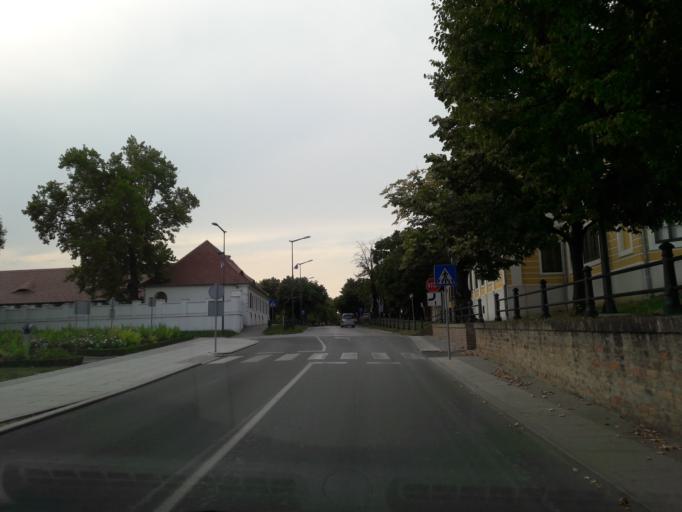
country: HR
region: Vukovarsko-Srijemska
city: Vukovar
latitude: 45.3541
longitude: 19.0005
